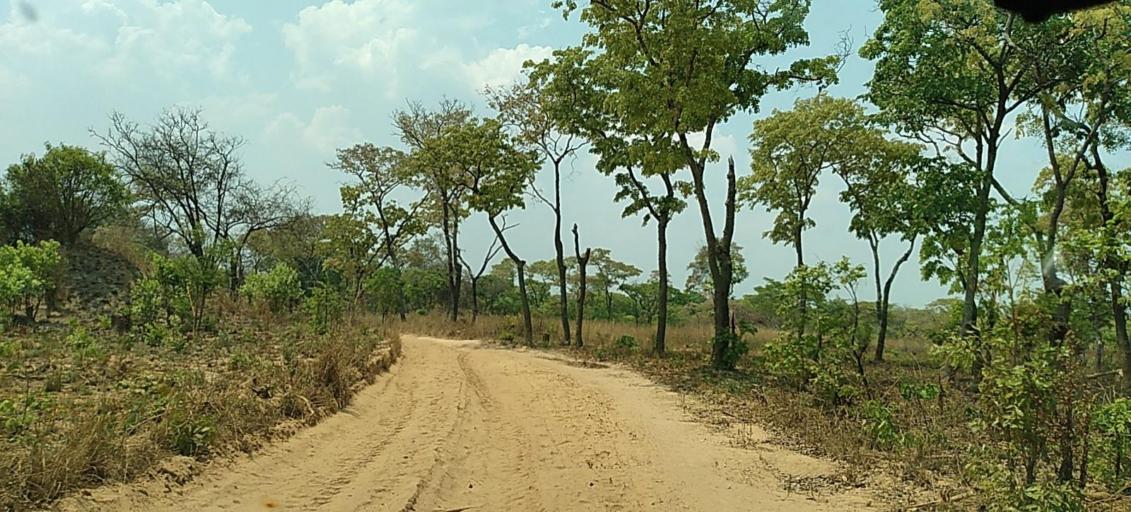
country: ZM
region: North-Western
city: Kabompo
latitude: -13.6371
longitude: 24.3846
